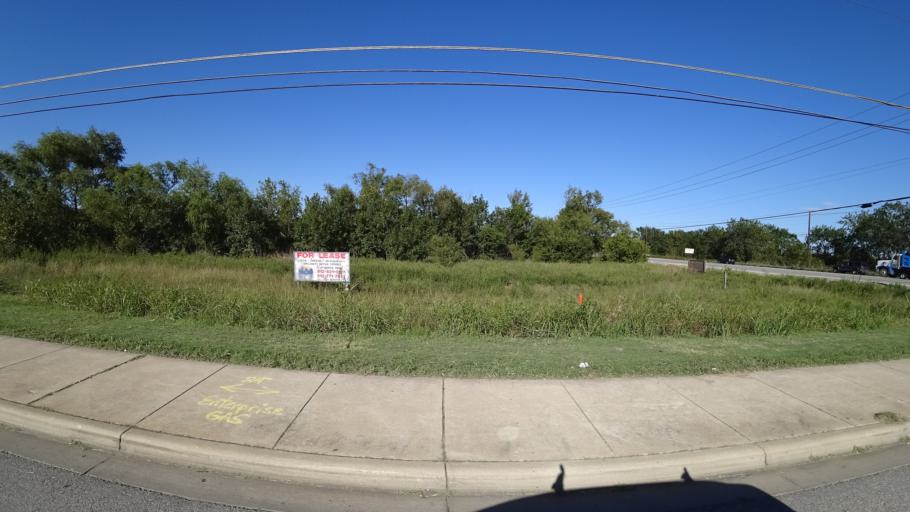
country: US
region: Texas
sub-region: Travis County
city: Hornsby Bend
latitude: 30.2915
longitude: -97.6283
